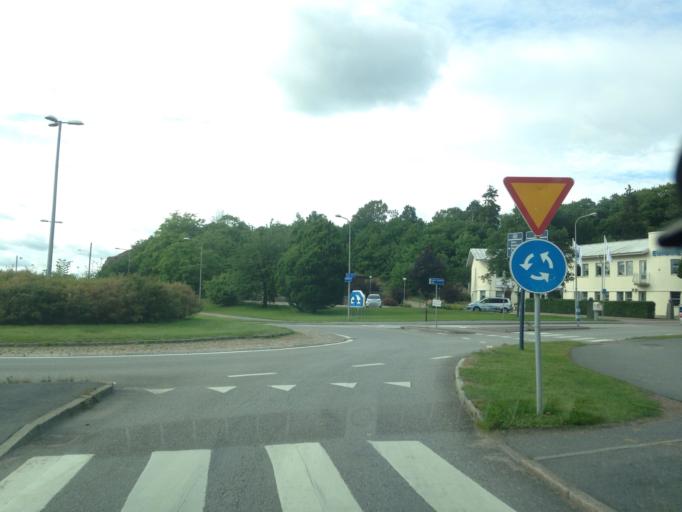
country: SE
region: Vaestra Goetaland
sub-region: Goteborg
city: Goeteborg
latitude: 57.7468
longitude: 11.9513
